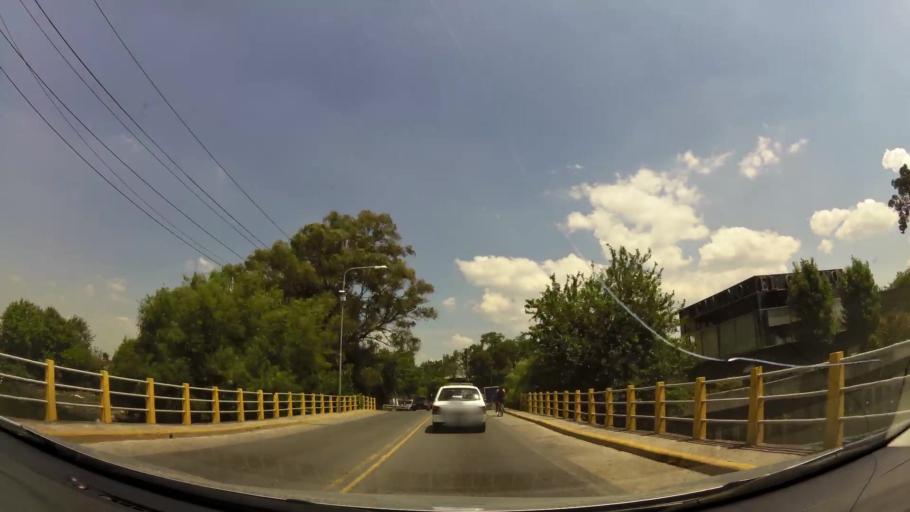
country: AR
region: Buenos Aires
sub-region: Partido de Tigre
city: Tigre
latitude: -34.4417
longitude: -58.5970
